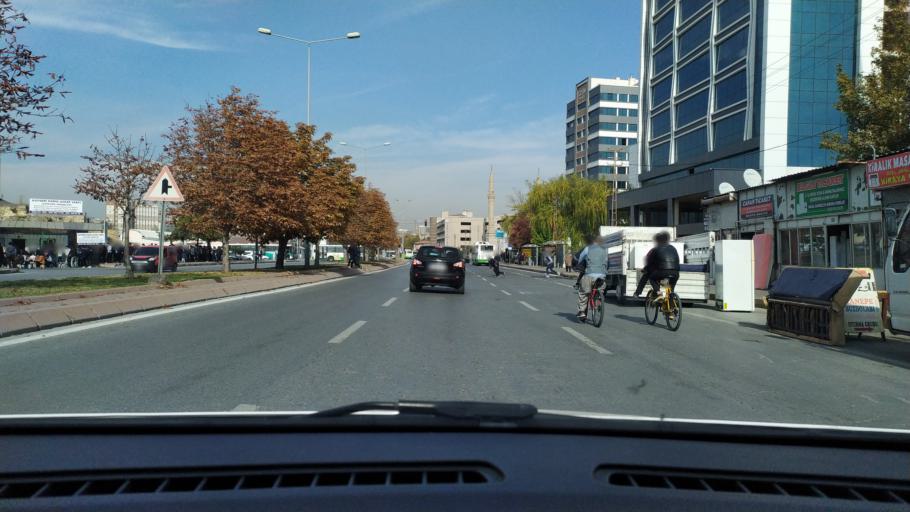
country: TR
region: Kayseri
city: Kayseri
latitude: 38.7130
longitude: 35.4912
